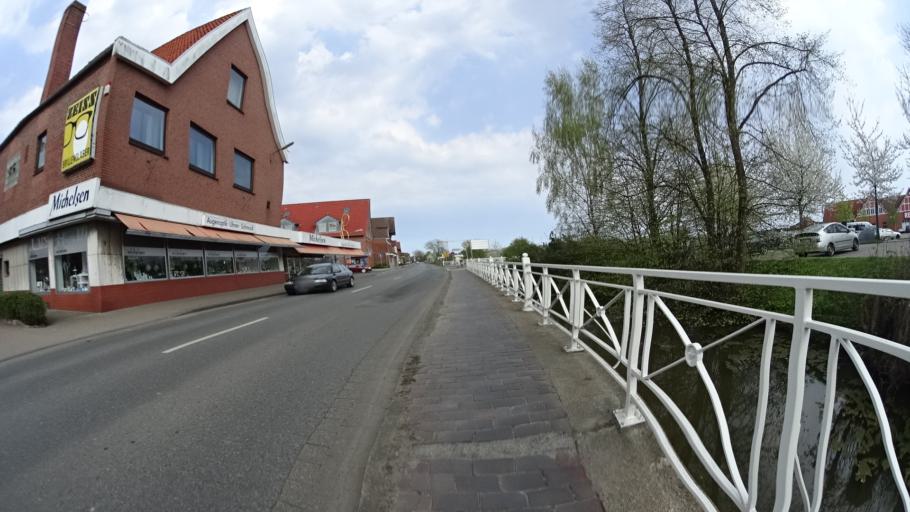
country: DE
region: Lower Saxony
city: Jork
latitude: 53.5332
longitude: 9.6809
